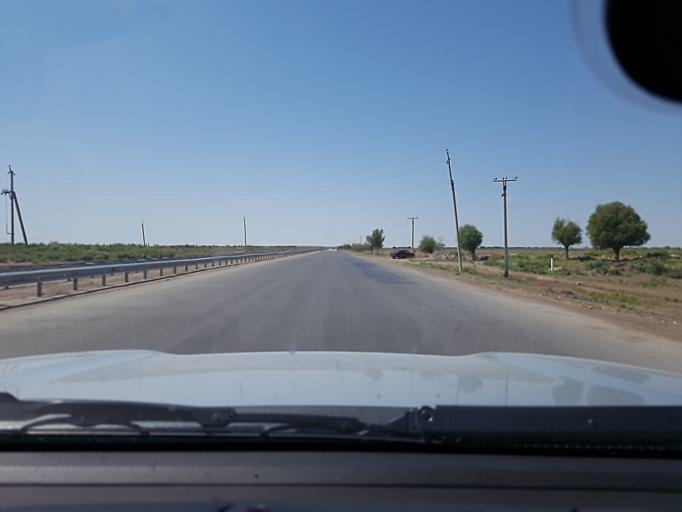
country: TM
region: Dasoguz
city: Yylanly
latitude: 41.7587
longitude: 59.4128
